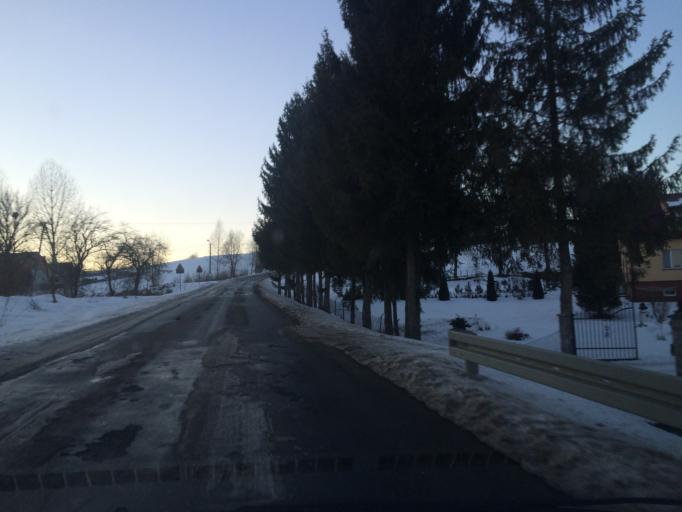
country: PL
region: Subcarpathian Voivodeship
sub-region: Powiat bieszczadzki
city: Ustrzyki Dolne
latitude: 49.3932
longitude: 22.6236
